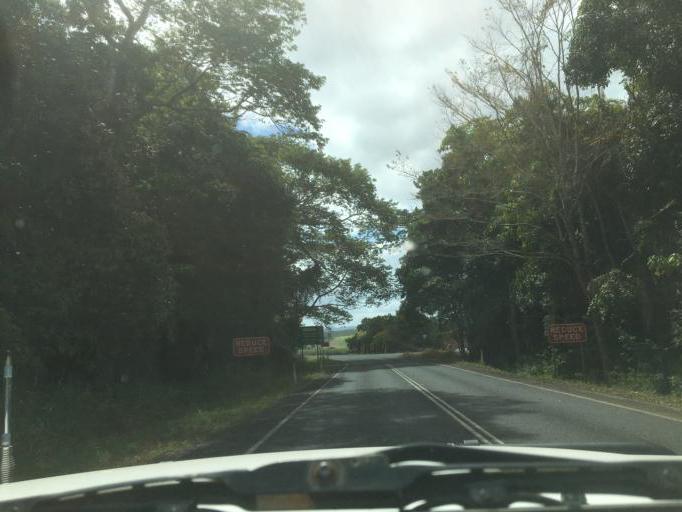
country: AU
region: Queensland
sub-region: Tablelands
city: Tolga
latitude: -17.2808
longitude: 145.6114
